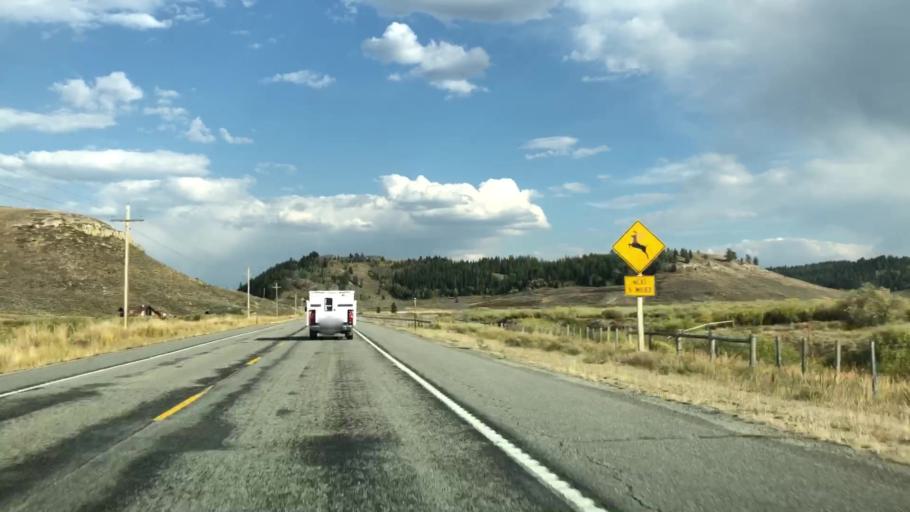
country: US
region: Wyoming
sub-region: Teton County
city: Hoback
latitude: 43.1550
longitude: -110.3458
